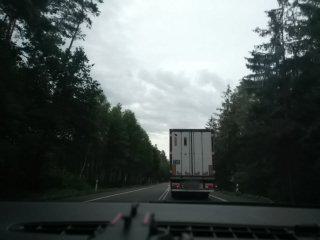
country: PL
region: Lublin Voivodeship
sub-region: Powiat janowski
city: Modliborzyce
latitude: 50.6767
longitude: 22.3375
